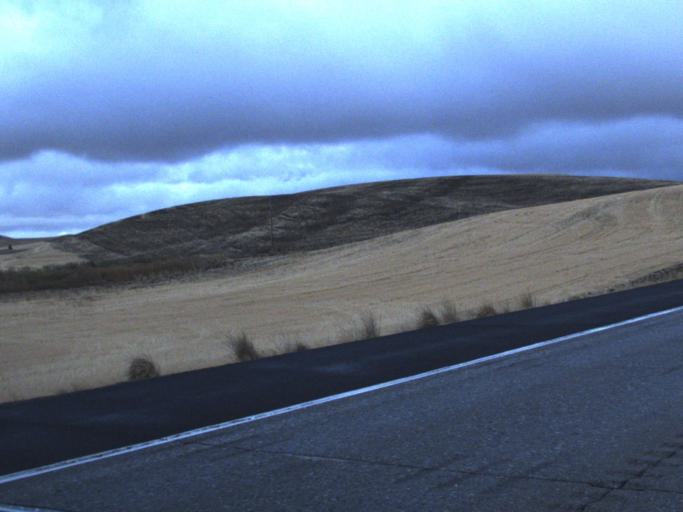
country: US
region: Washington
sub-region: Whitman County
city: Colfax
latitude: 47.0557
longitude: -117.3808
